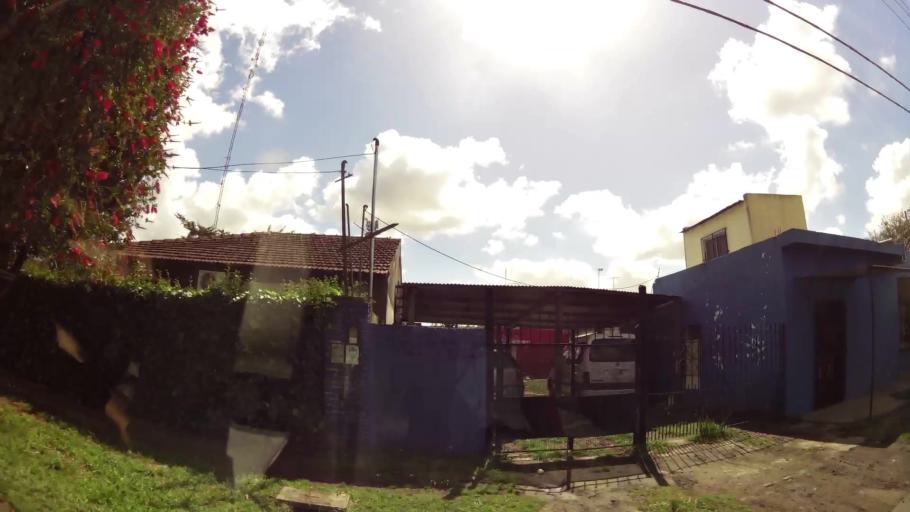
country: AR
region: Buenos Aires
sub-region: Partido de Quilmes
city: Quilmes
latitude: -34.8345
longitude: -58.1791
